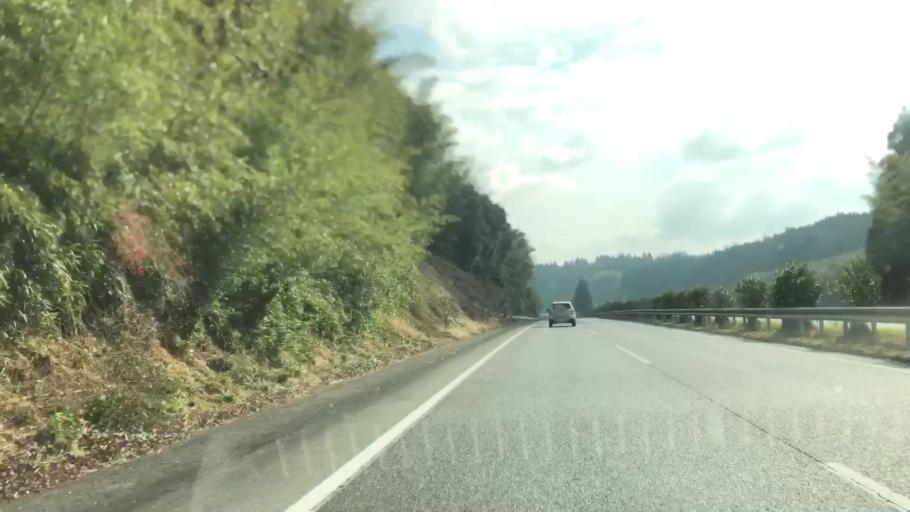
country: JP
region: Kumamoto
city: Yamaga
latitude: 33.0360
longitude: 130.5717
